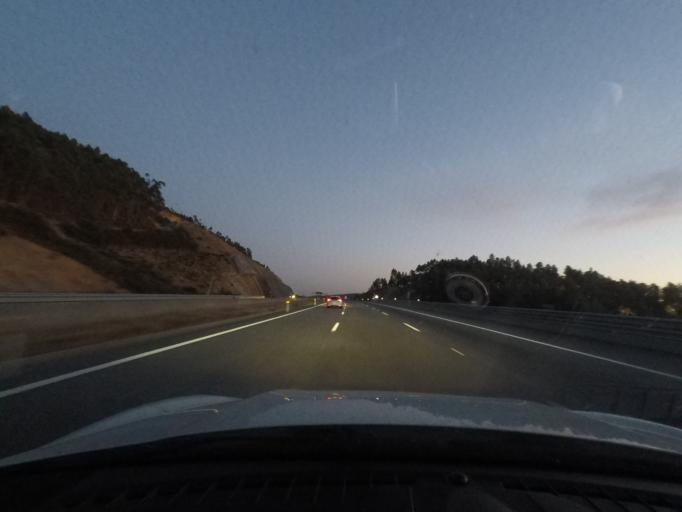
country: PT
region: Porto
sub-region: Paredes
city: Recarei
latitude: 41.1217
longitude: -8.4335
